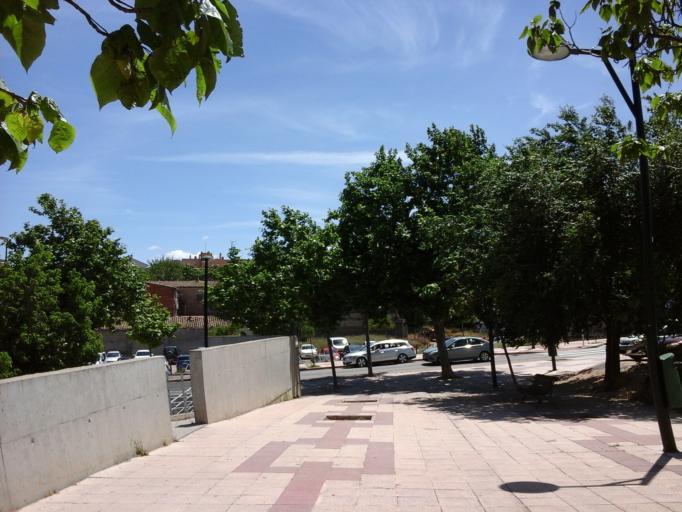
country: ES
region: Aragon
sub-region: Provincia de Zaragoza
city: Zaragoza
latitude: 41.6307
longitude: -0.8790
